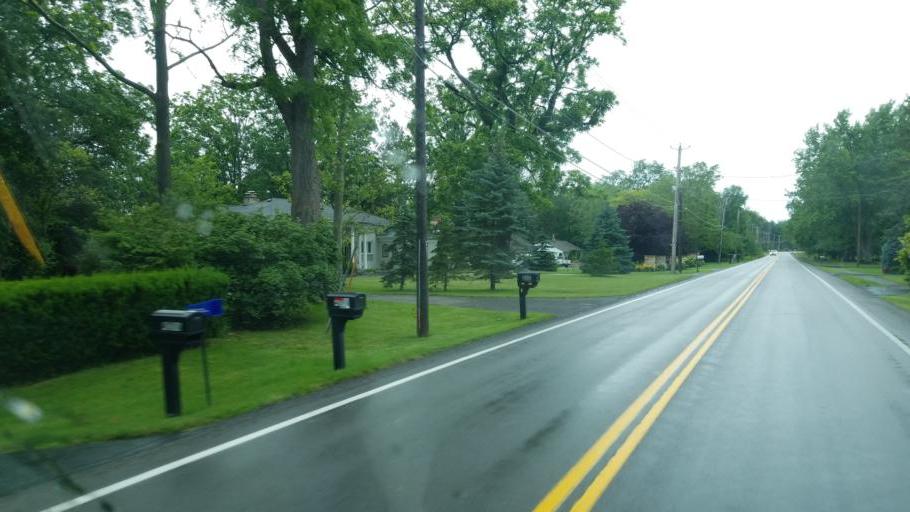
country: US
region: New York
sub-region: Niagara County
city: Lewiston
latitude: 43.2051
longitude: -79.0446
